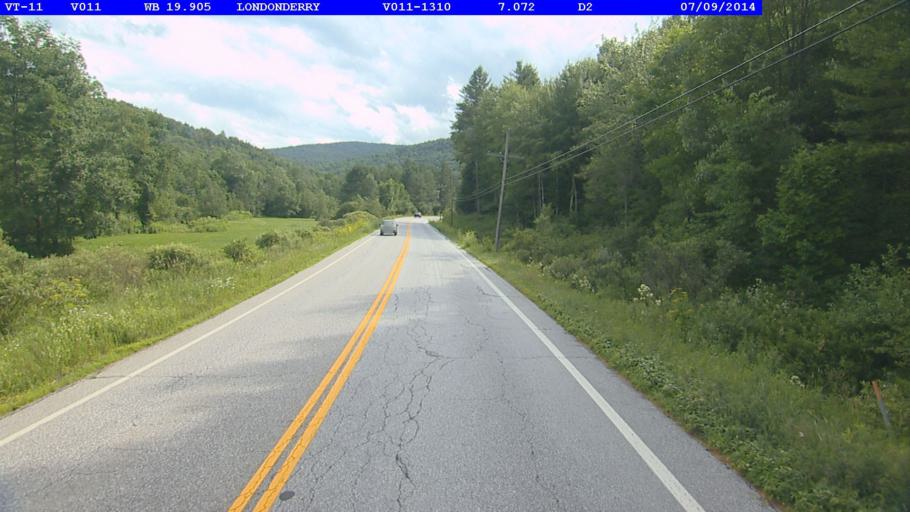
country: US
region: Vermont
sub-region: Windsor County
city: Chester
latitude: 43.2227
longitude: -72.7351
